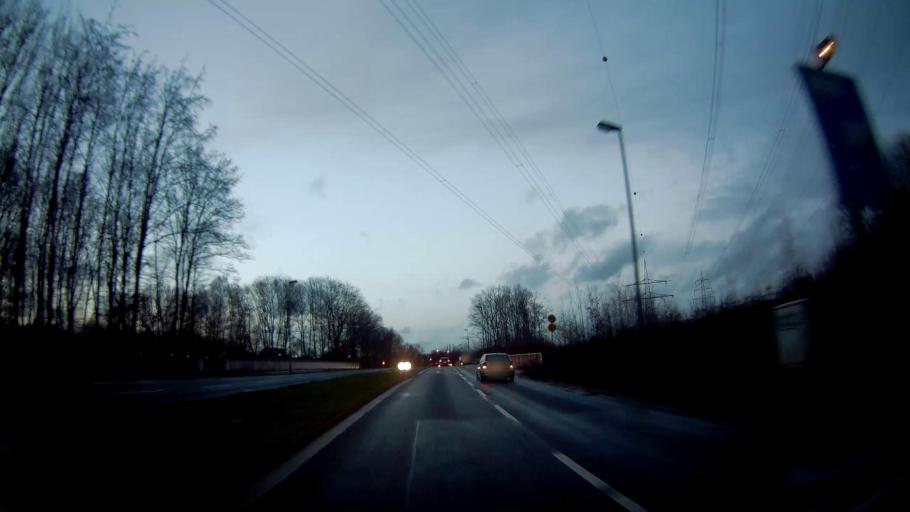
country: DE
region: North Rhine-Westphalia
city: Castrop-Rauxel
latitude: 51.4960
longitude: 7.2894
